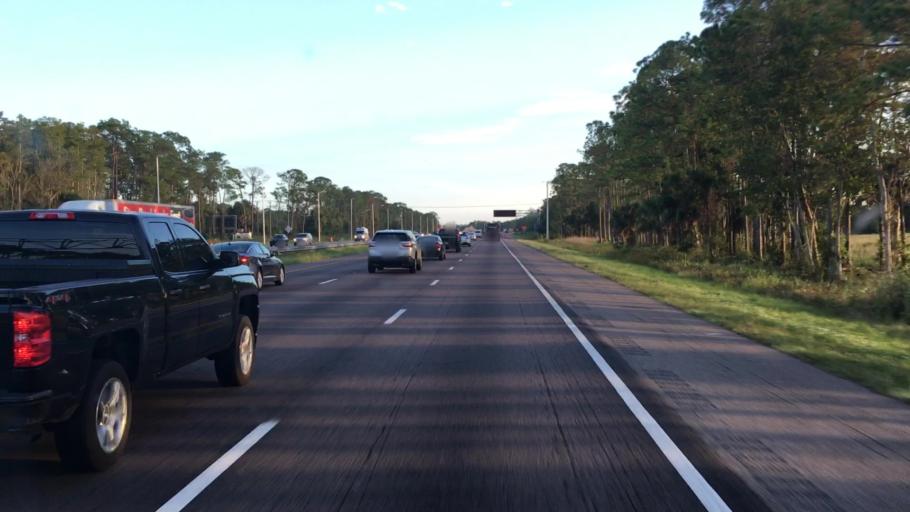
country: US
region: Florida
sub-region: Volusia County
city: Daytona Beach
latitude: 29.1868
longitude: -81.0918
